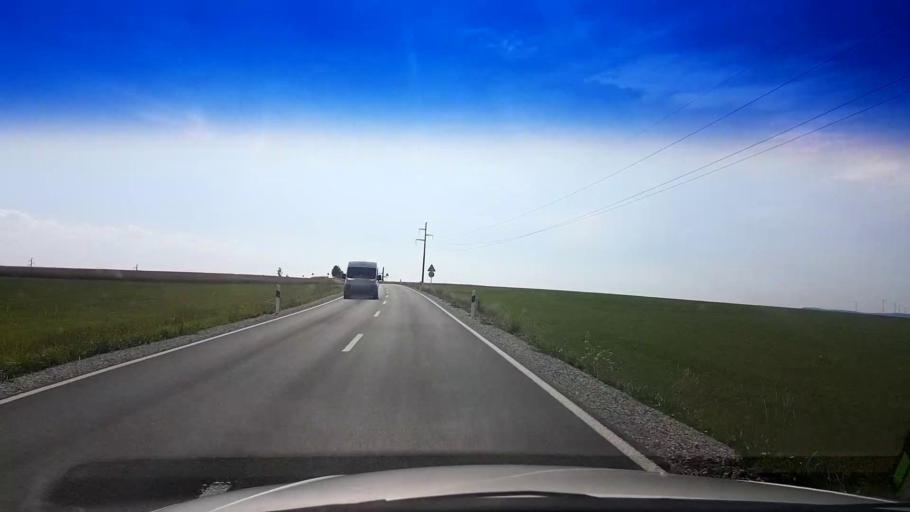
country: DE
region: Bavaria
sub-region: Upper Franconia
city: Mistelgau
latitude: 49.9365
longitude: 11.4669
